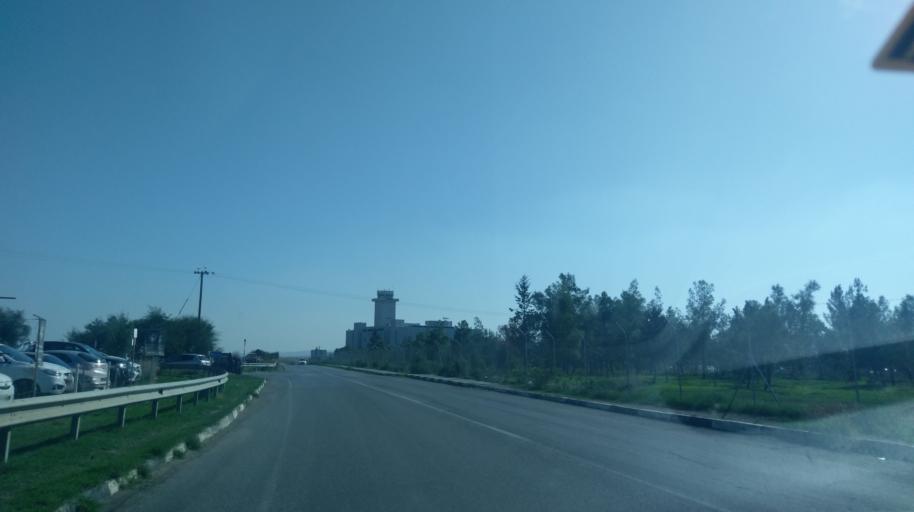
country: CY
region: Lefkosia
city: Geri
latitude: 35.1594
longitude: 33.5050
